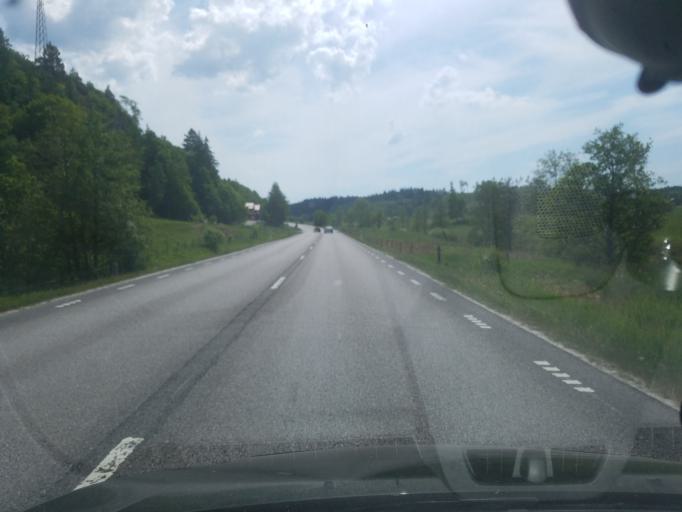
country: SE
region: Vaestra Goetaland
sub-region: Orust
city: Henan
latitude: 58.2047
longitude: 11.6900
